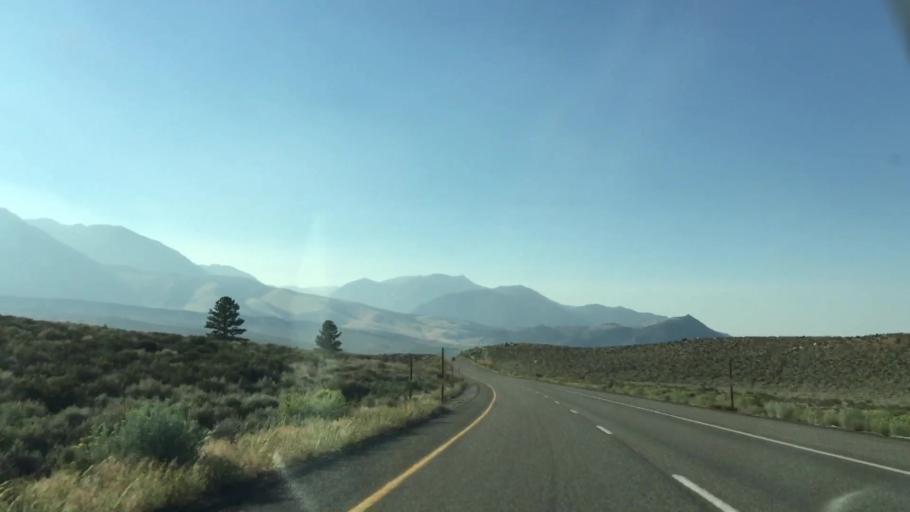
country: US
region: California
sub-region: Mono County
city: Mammoth Lakes
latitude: 37.8431
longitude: -119.0727
